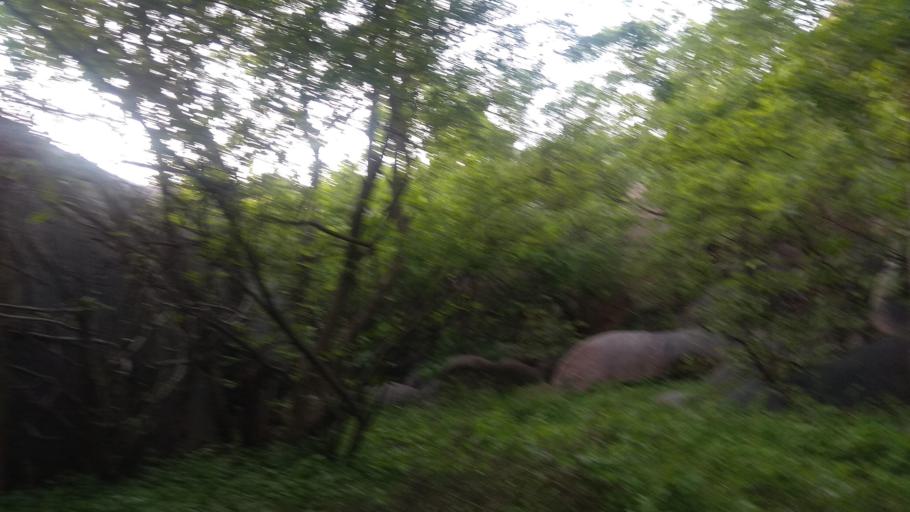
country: IN
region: Telangana
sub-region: Mahbubnagar
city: Farrukhnagar
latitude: 16.8986
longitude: 78.4917
